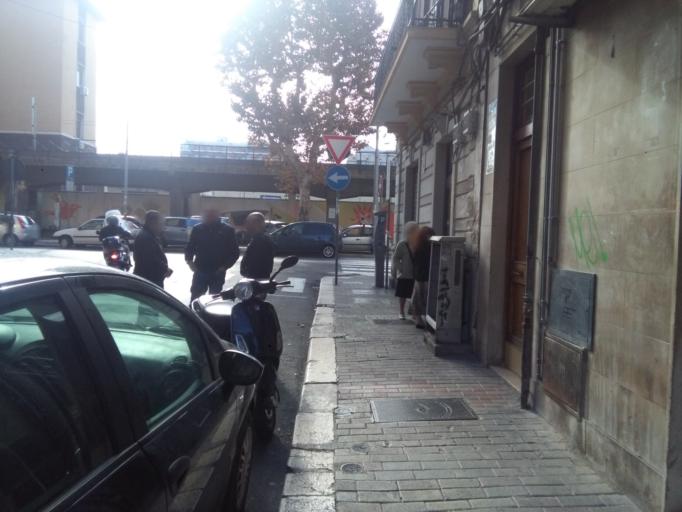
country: IT
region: Apulia
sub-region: Provincia di Bari
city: Bari
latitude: 41.1184
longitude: 16.8611
